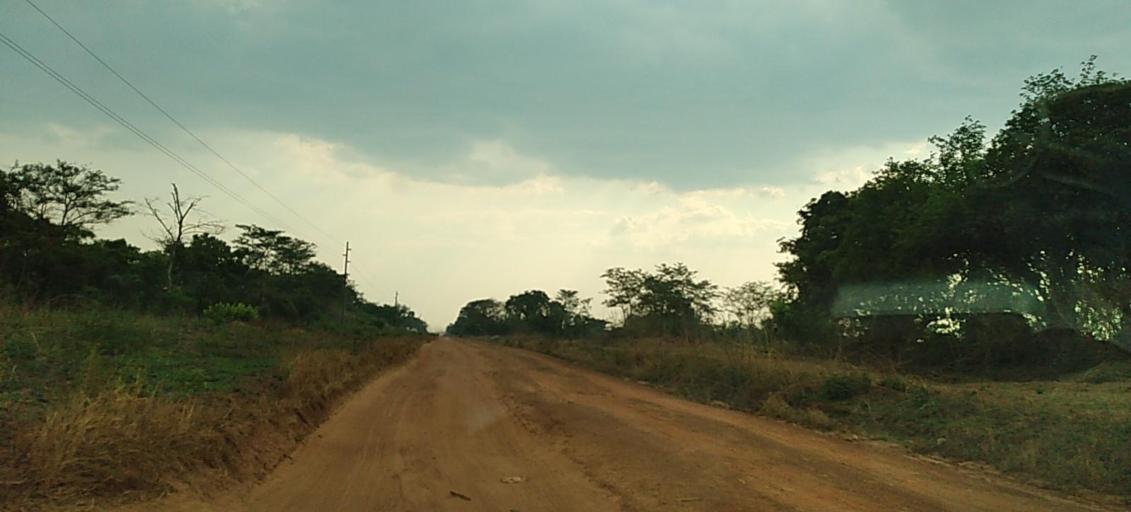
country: ZM
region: Copperbelt
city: Kalulushi
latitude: -12.9397
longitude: 27.9243
